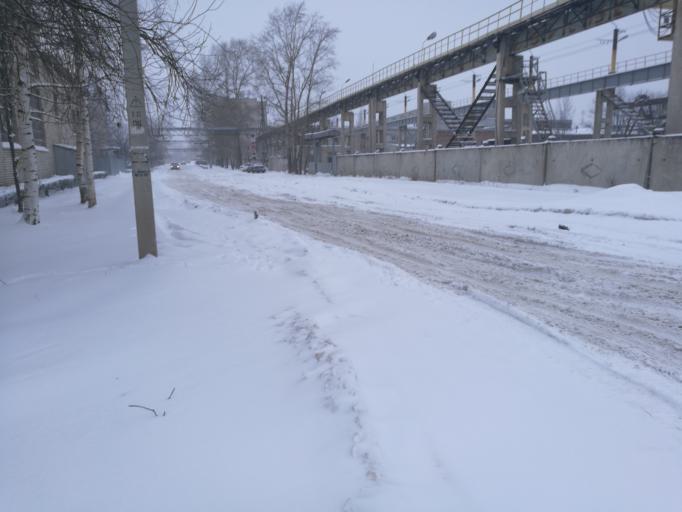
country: RU
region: Vologda
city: Vologda
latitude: 59.2060
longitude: 39.8699
